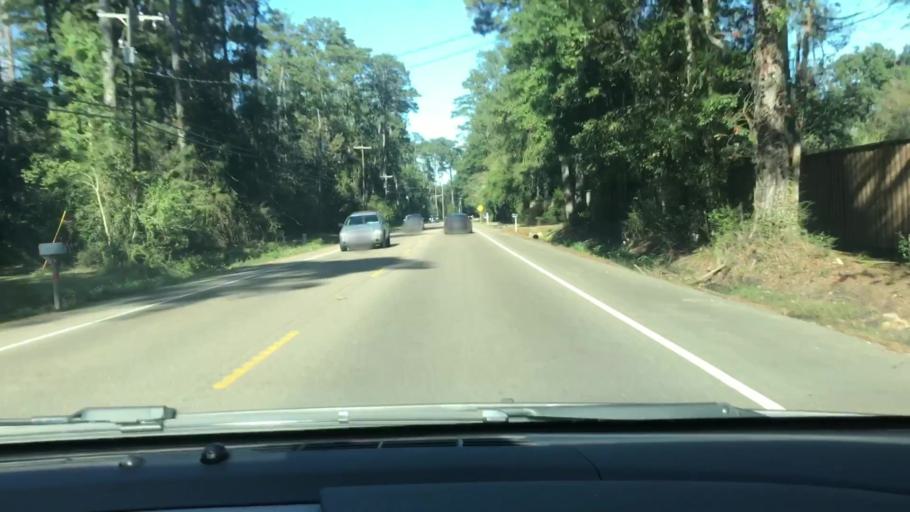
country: US
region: Louisiana
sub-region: Saint Tammany Parish
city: Covington
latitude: 30.4825
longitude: -90.0815
